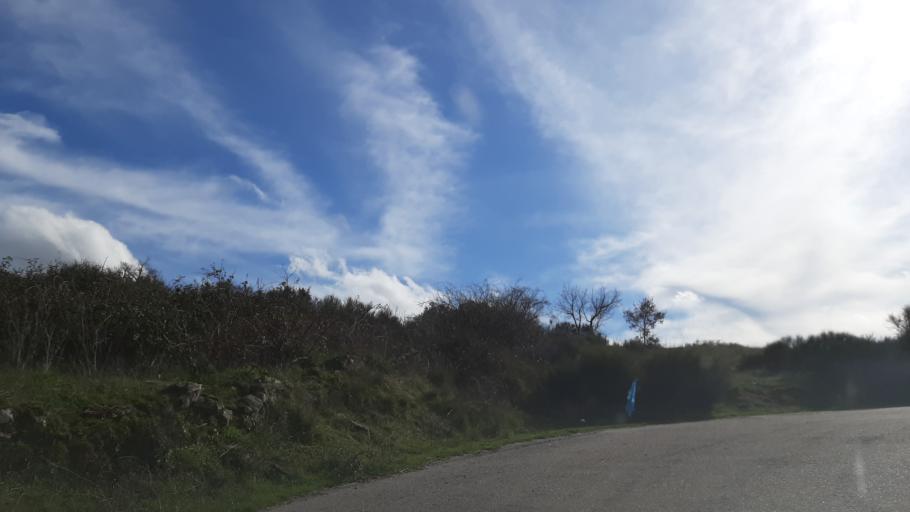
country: ES
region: Castille and Leon
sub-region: Provincia de Salamanca
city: Villarino de los Aires
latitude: 41.2552
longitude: -6.5266
